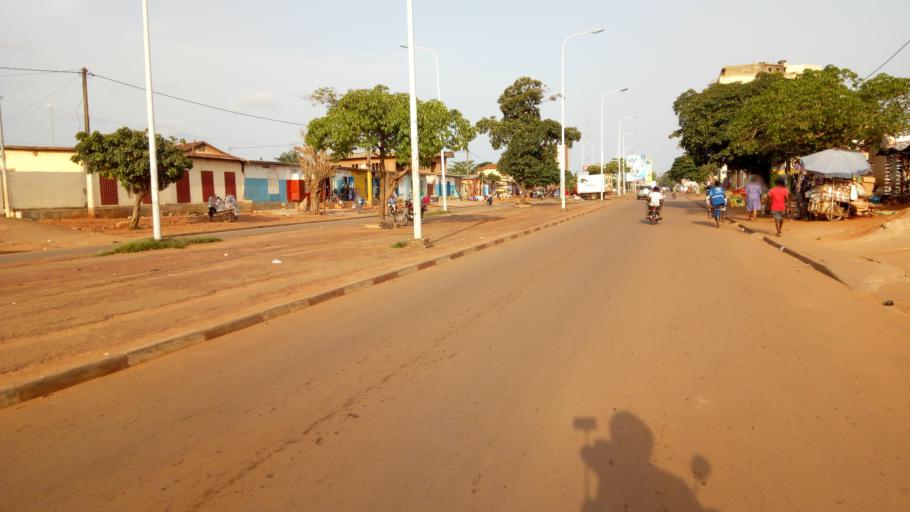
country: BJ
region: Queme
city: Porto-Novo
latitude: 6.4844
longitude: 2.6174
